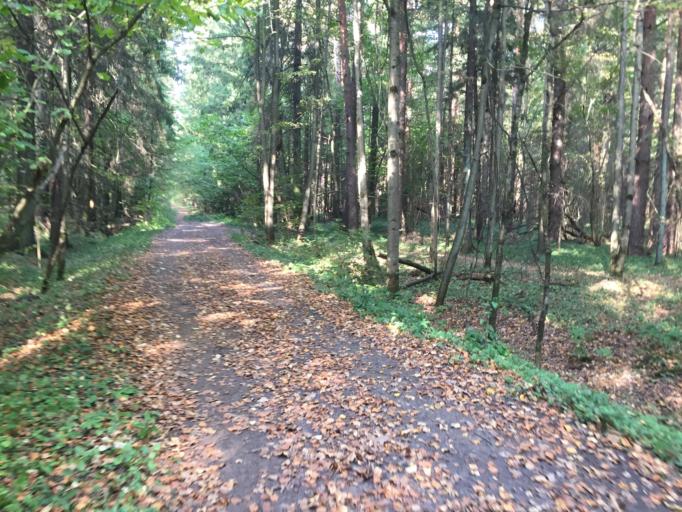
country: RU
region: Moscow
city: Babushkin
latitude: 55.8617
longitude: 37.7431
